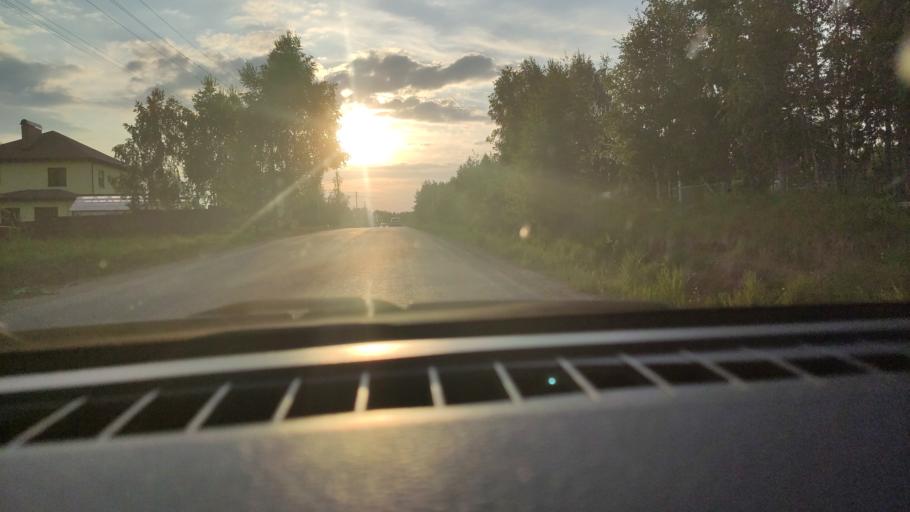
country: RU
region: Perm
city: Kondratovo
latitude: 58.0562
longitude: 56.0124
